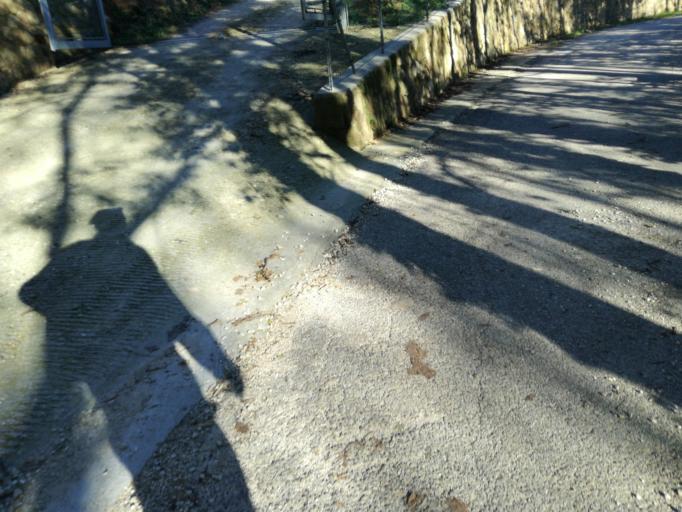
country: IT
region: Veneto
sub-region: Provincia di Padova
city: Arqua Petrarca
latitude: 45.2754
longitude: 11.7332
